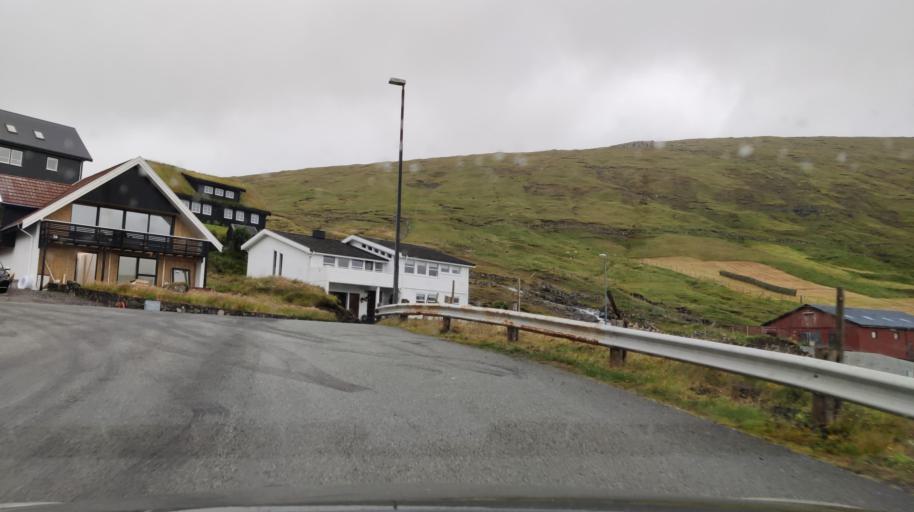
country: FO
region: Streymoy
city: Vestmanna
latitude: 62.1574
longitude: -7.1771
